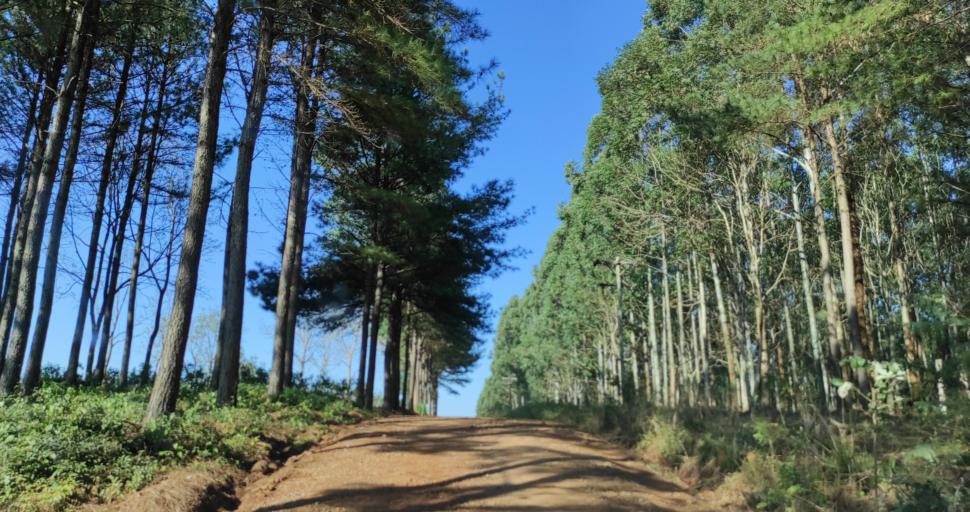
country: AR
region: Misiones
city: Capiovi
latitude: -26.8879
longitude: -55.0378
